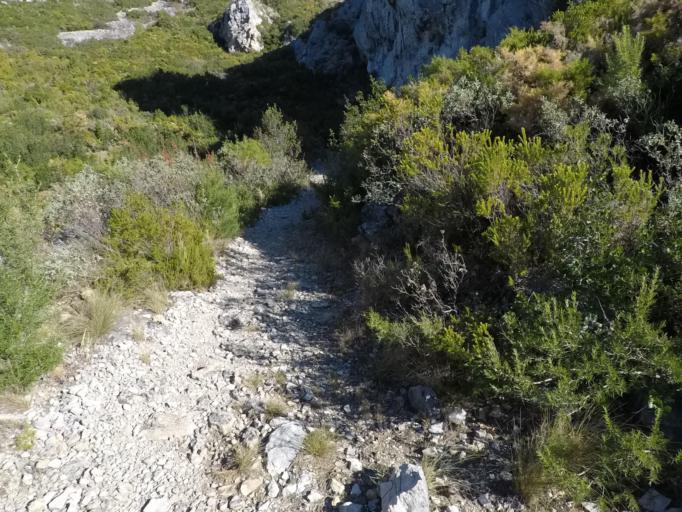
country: FR
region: Provence-Alpes-Cote d'Azur
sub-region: Departement des Bouches-du-Rhone
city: La Penne-sur-Huveaune
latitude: 43.2695
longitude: 5.4895
